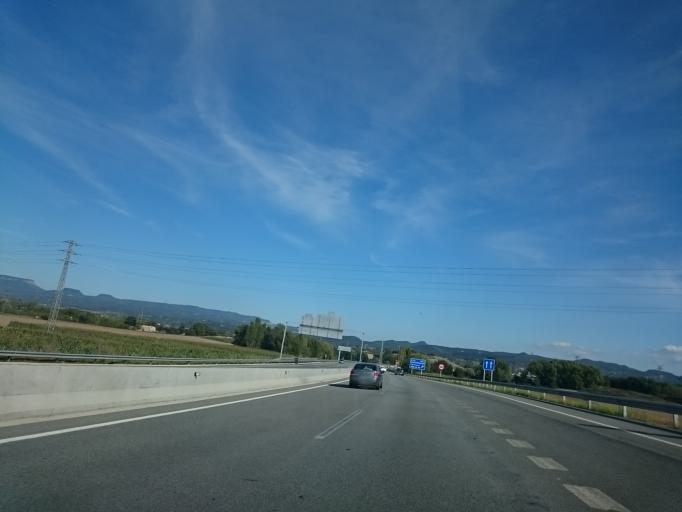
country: ES
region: Catalonia
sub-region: Provincia de Barcelona
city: Vic
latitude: 41.9602
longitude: 2.2705
